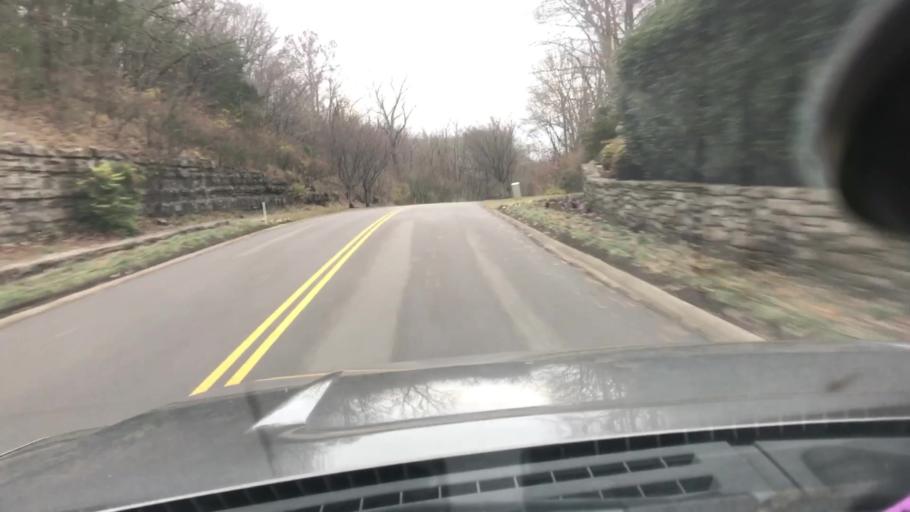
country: US
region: Tennessee
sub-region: Williamson County
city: Brentwood Estates
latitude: 35.9661
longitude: -86.7557
